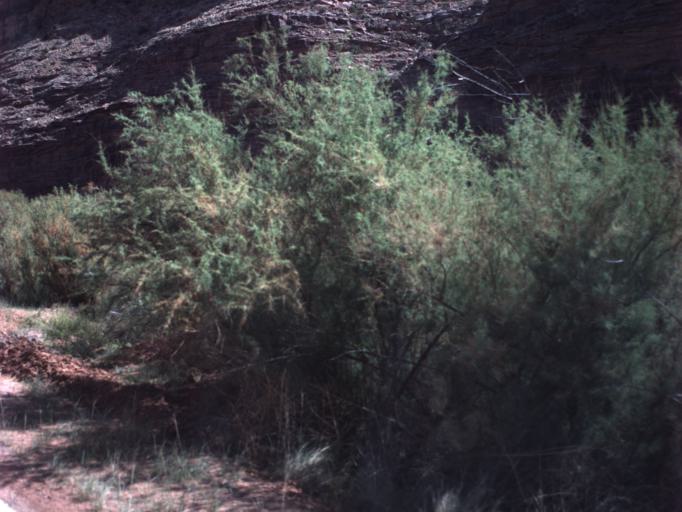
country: US
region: Utah
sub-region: Grand County
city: Moab
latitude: 38.5307
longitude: -109.6165
